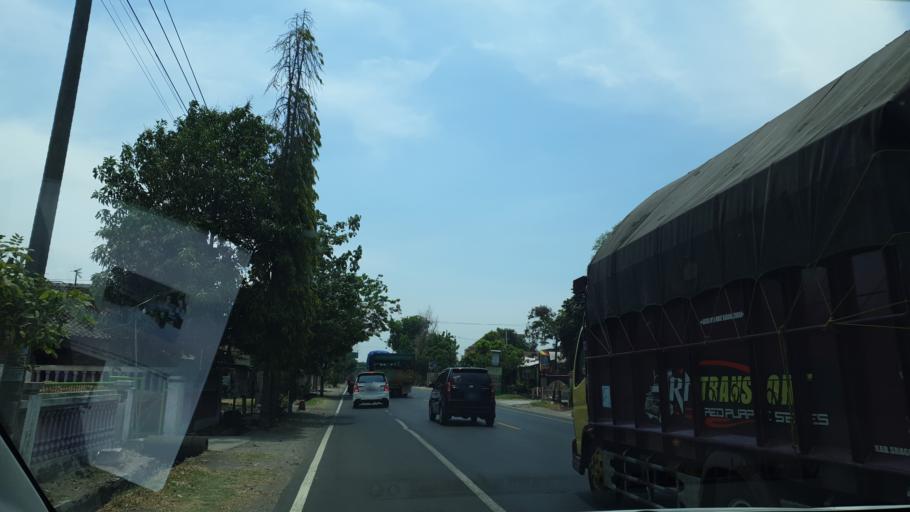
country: ID
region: East Java
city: Nganjuk
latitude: -7.6025
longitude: 111.9474
